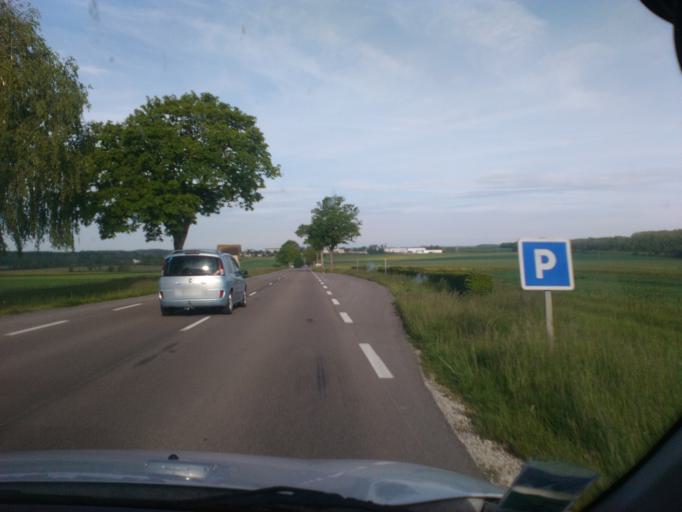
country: FR
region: Champagne-Ardenne
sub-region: Departement de l'Aube
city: Vendeuvre-sur-Barse
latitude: 48.2369
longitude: 4.5016
